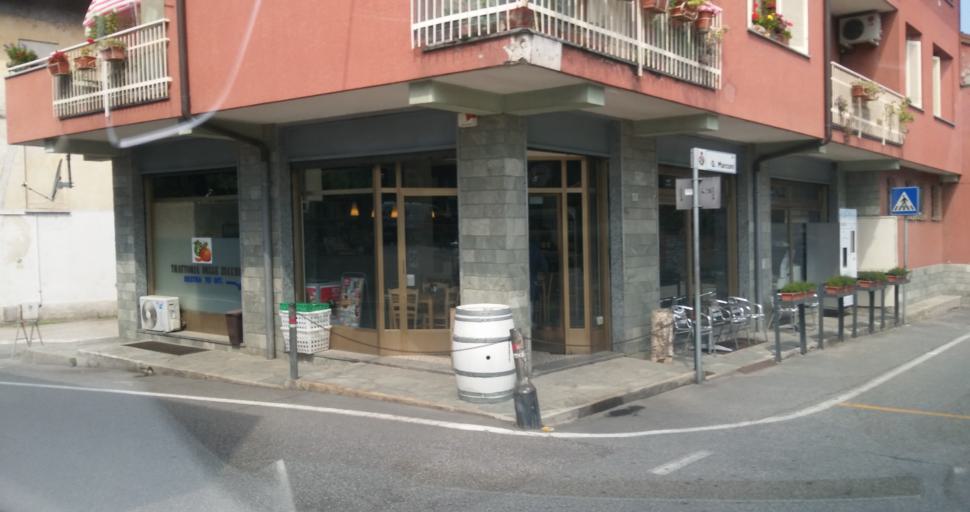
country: IT
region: Lombardy
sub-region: Provincia di Varese
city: Osmate
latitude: 45.7893
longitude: 8.6592
